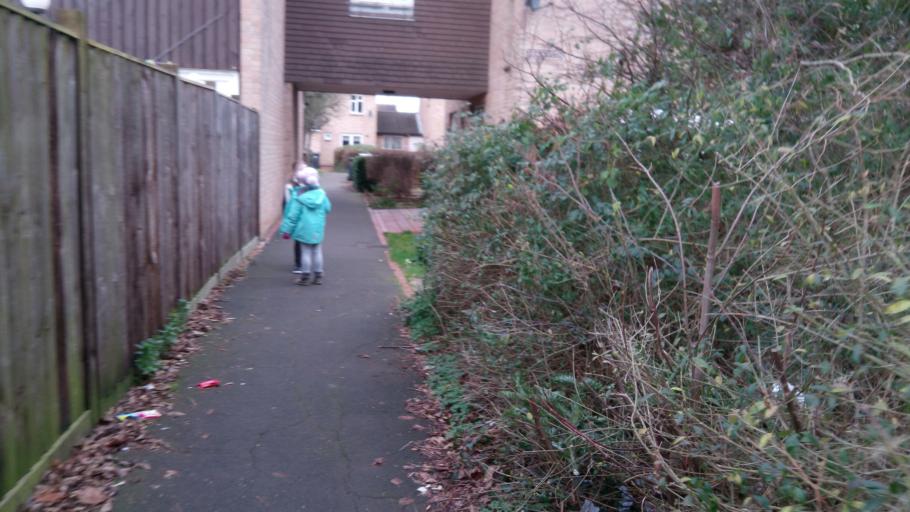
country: GB
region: England
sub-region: Peterborough
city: Marholm
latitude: 52.5776
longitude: -0.2864
